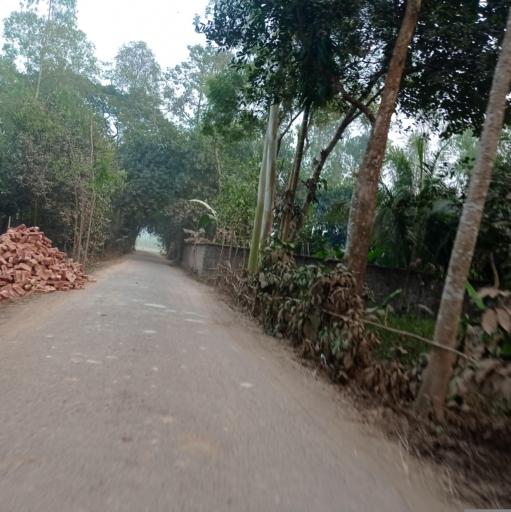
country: BD
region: Dhaka
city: Bajitpur
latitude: 24.1313
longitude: 90.8197
